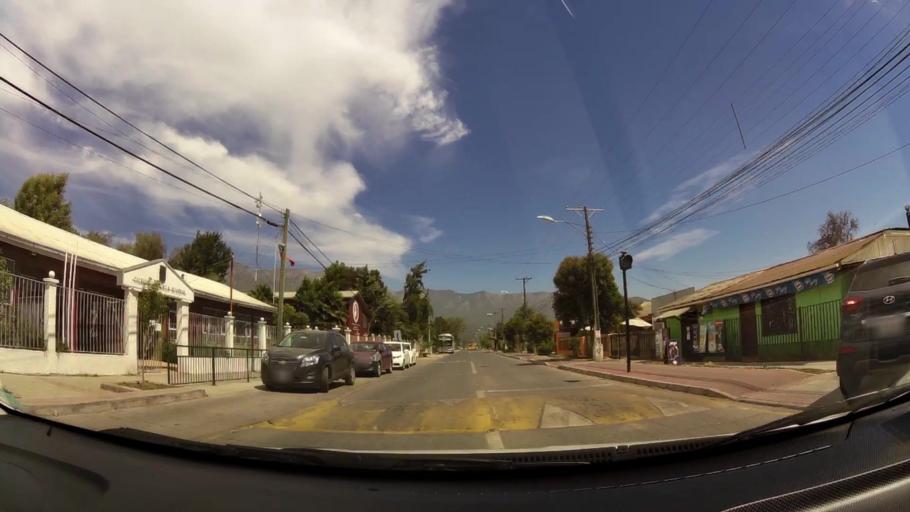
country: CL
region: O'Higgins
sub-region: Provincia de Cachapoal
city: Graneros
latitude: -33.9841
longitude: -70.7063
